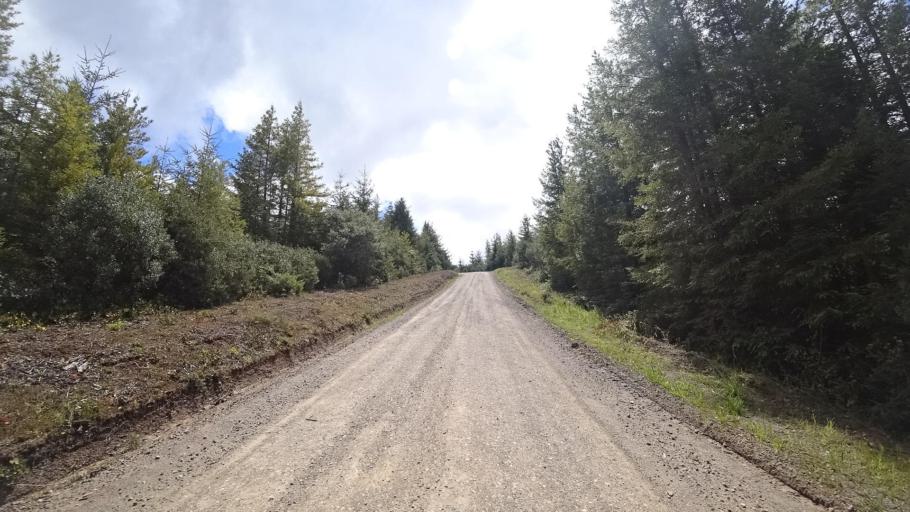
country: US
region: California
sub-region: Humboldt County
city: Blue Lake
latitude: 40.7725
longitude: -123.9619
